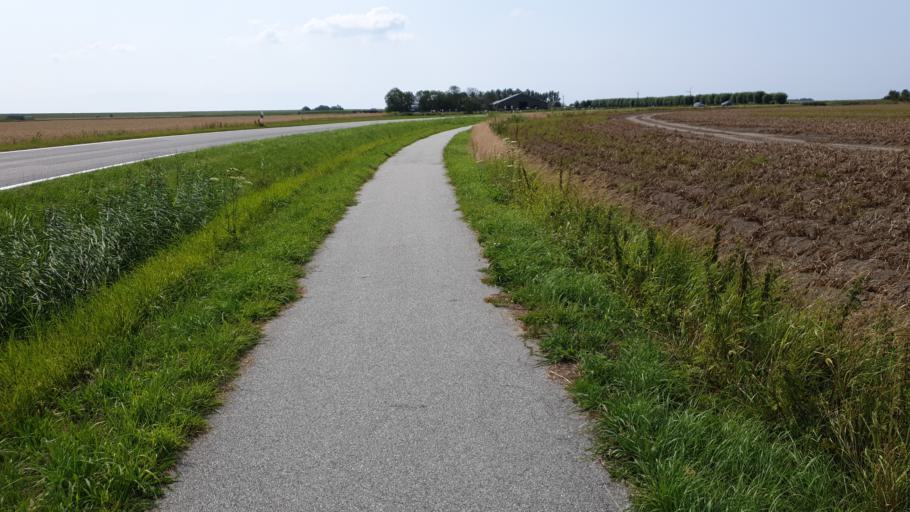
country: DE
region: Schleswig-Holstein
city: Elisabeth-Sophien-Koog
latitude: 54.4664
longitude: 8.8956
